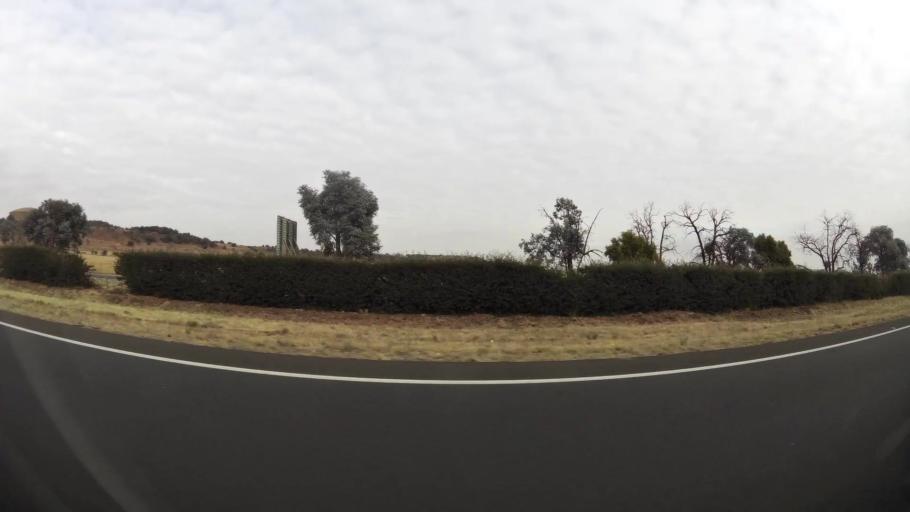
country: ZA
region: Orange Free State
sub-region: Mangaung Metropolitan Municipality
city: Bloemfontein
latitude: -29.1395
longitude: 26.1686
